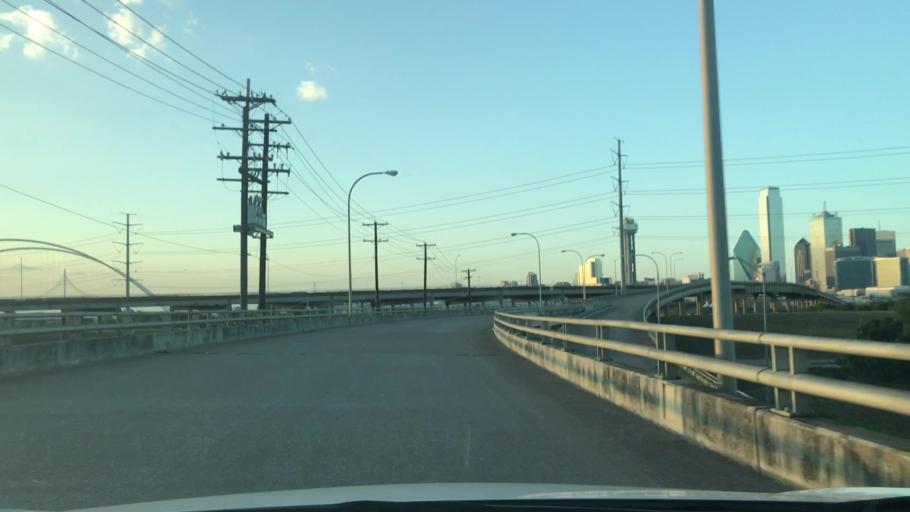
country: US
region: Texas
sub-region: Dallas County
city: Dallas
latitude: 32.7612
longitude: -96.8132
